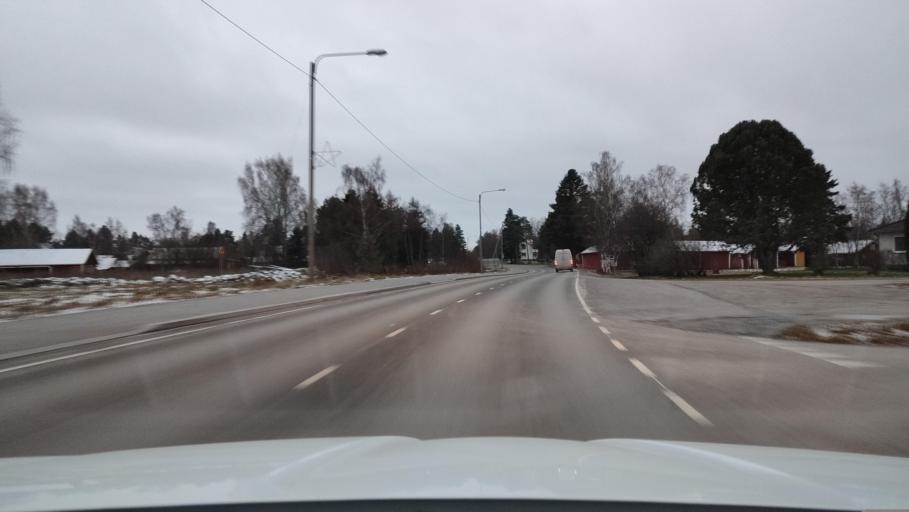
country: FI
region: Ostrobothnia
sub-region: Vaasa
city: Replot
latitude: 63.2304
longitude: 21.4105
